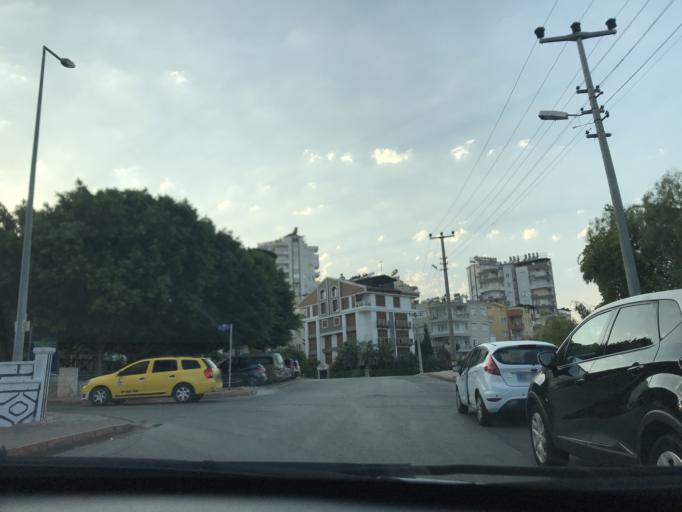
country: TR
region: Antalya
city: Antalya
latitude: 36.8772
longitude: 30.6446
